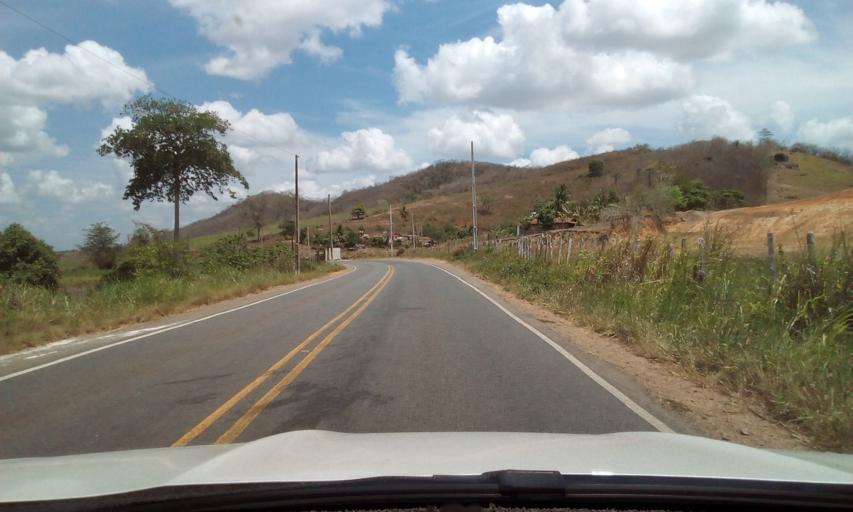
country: BR
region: Paraiba
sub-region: Alagoinha
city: Alagoinha
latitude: -6.9389
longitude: -35.5376
